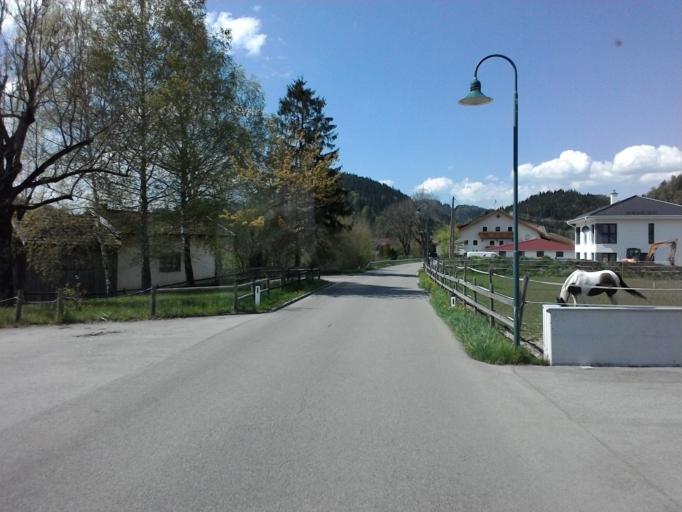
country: AT
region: Tyrol
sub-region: Politischer Bezirk Reutte
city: Musau
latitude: 47.5416
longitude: 10.6774
